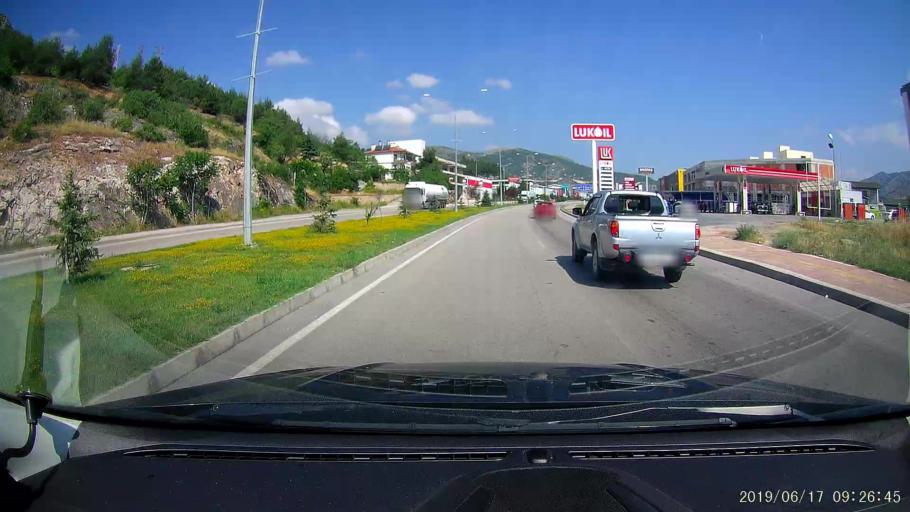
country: TR
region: Amasya
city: Amasya
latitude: 40.6711
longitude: 35.8322
